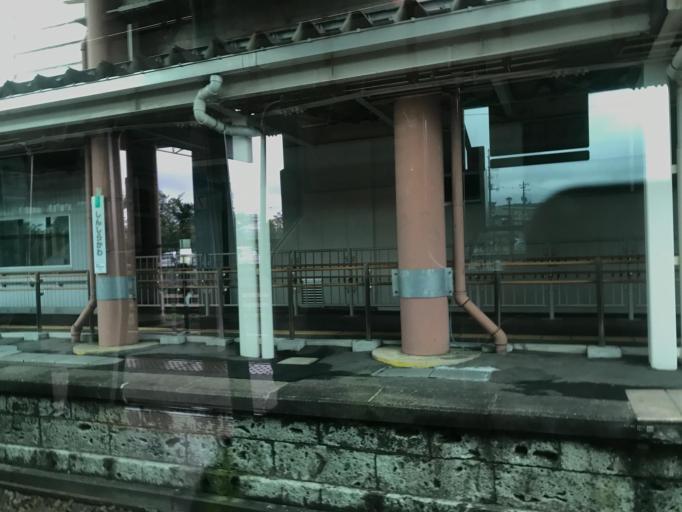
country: JP
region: Tochigi
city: Kuroiso
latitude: 37.1231
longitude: 140.1884
